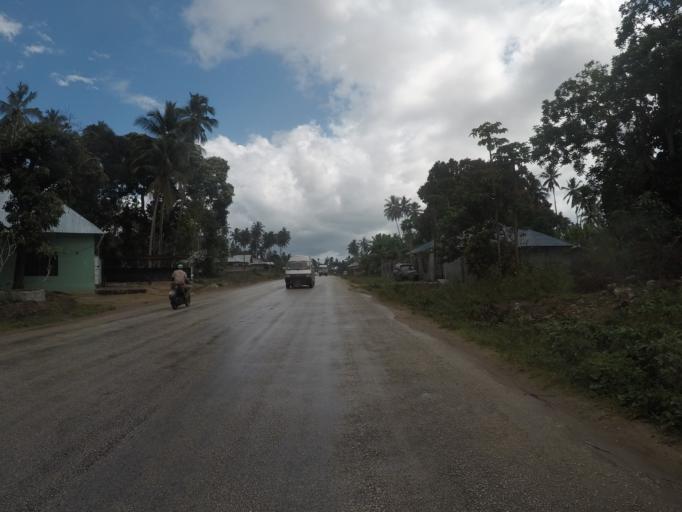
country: TZ
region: Zanzibar Central/South
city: Koani
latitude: -6.0231
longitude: 39.2405
